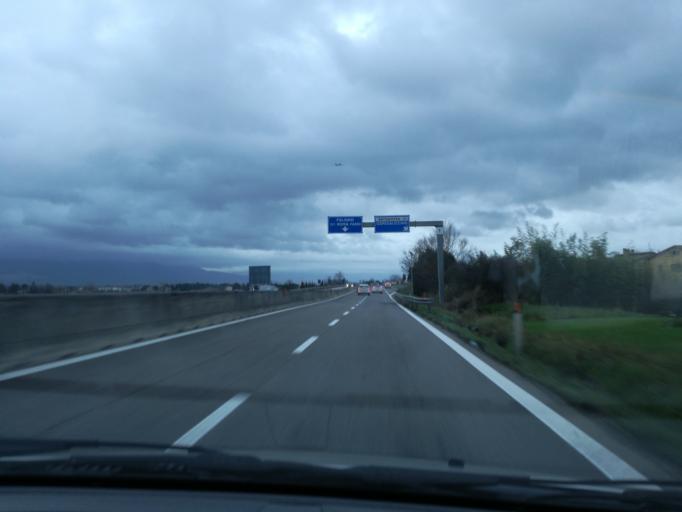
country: IT
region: Umbria
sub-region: Provincia di Perugia
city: Via Lippia
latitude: 43.0863
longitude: 12.4834
